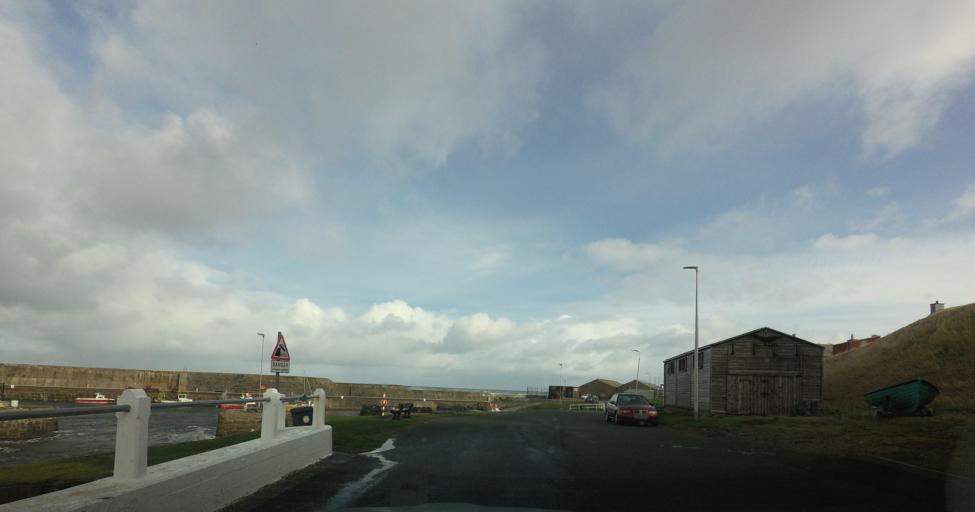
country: GB
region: Scotland
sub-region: Aberdeenshire
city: Portsoy
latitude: 57.6854
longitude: -2.6889
